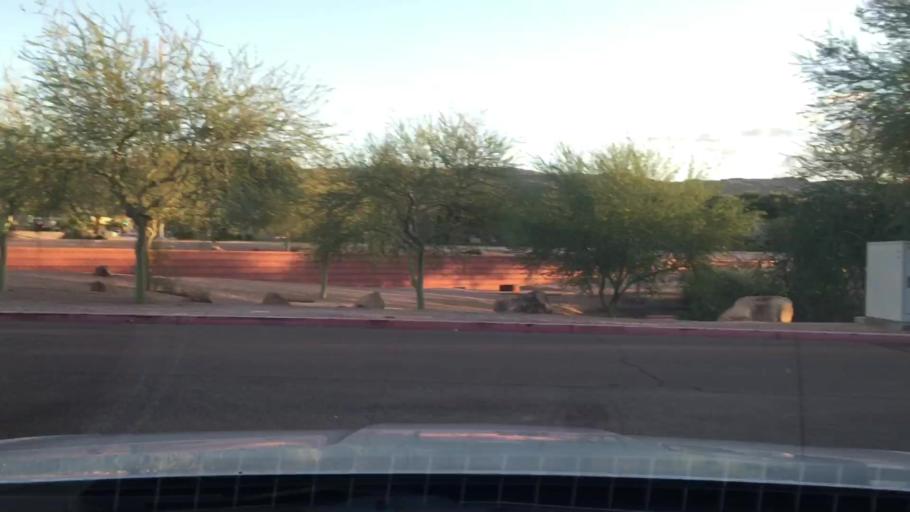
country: US
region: Arizona
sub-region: Maricopa County
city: Guadalupe
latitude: 33.3817
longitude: -112.0310
